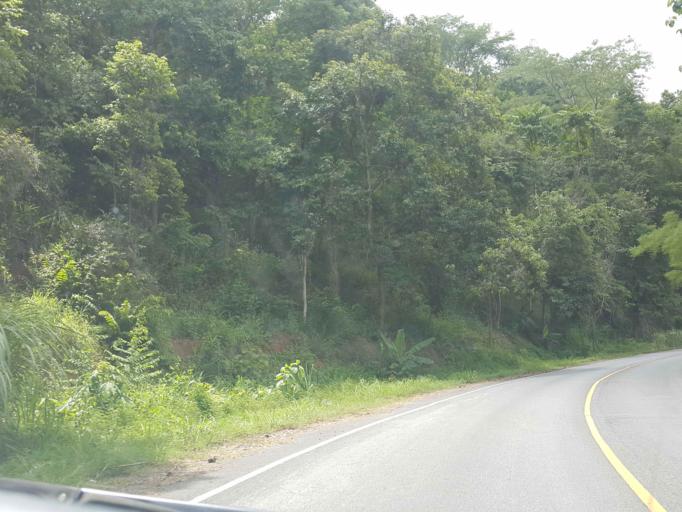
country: TH
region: Chiang Mai
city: Samoeng
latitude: 18.8106
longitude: 98.7890
